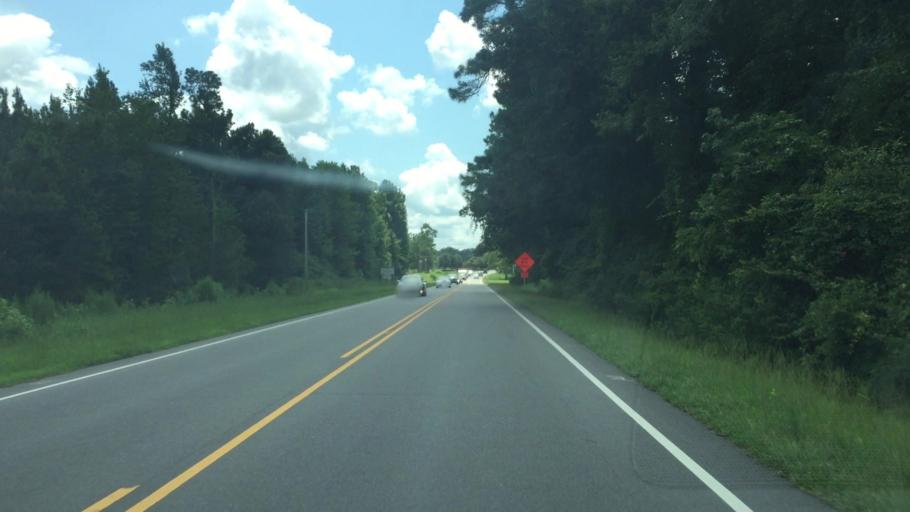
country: US
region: North Carolina
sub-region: Columbus County
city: Chadbourn
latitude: 34.2512
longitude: -78.8189
